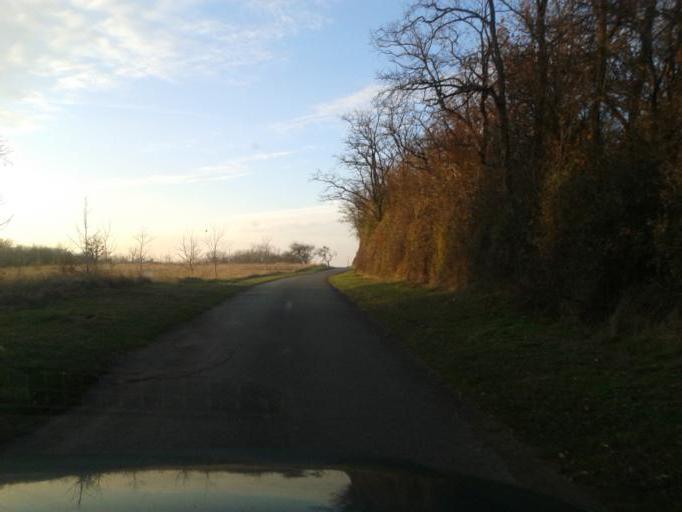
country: FR
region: Centre
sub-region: Departement du Loiret
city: Tavers
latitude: 47.7646
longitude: 1.5994
